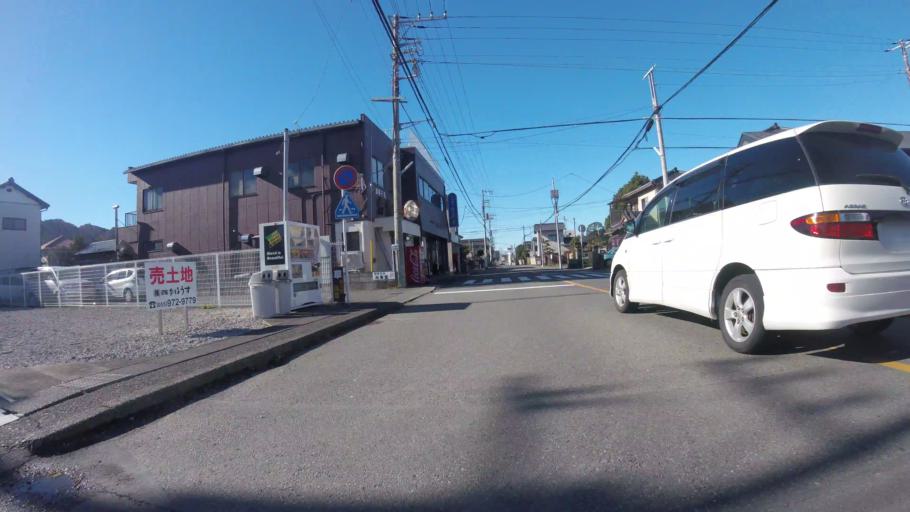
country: JP
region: Shizuoka
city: Numazu
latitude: 35.1049
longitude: 138.8842
